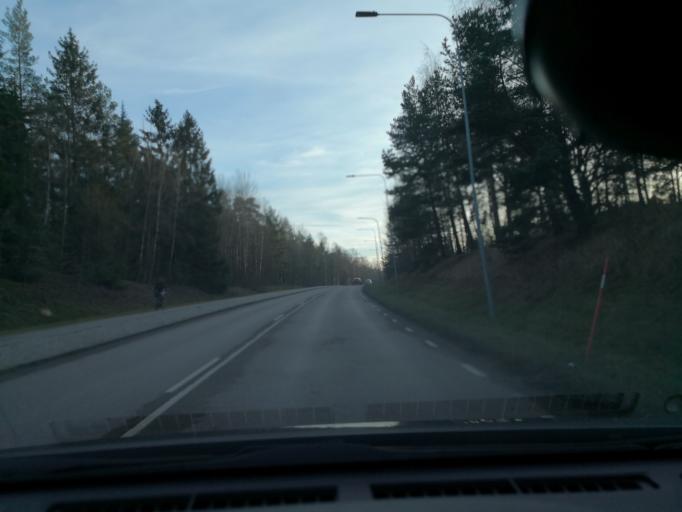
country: SE
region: Vaestmanland
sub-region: Vasteras
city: Vasteras
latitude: 59.6159
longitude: 16.5058
